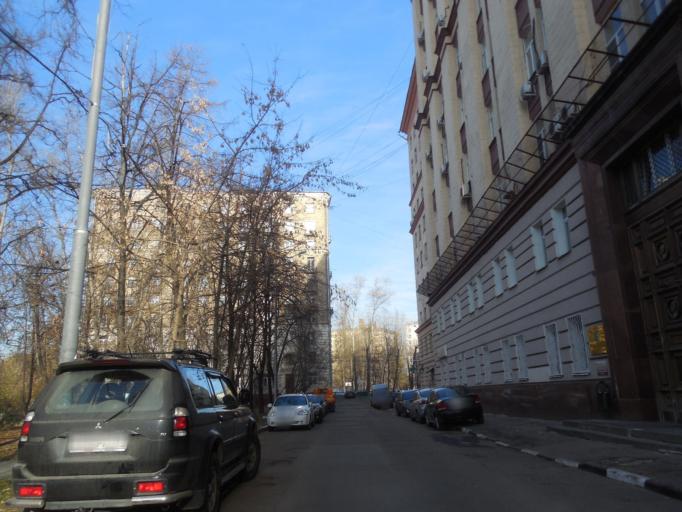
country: RU
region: Moscow
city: Lefortovo
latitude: 55.7772
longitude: 37.7044
